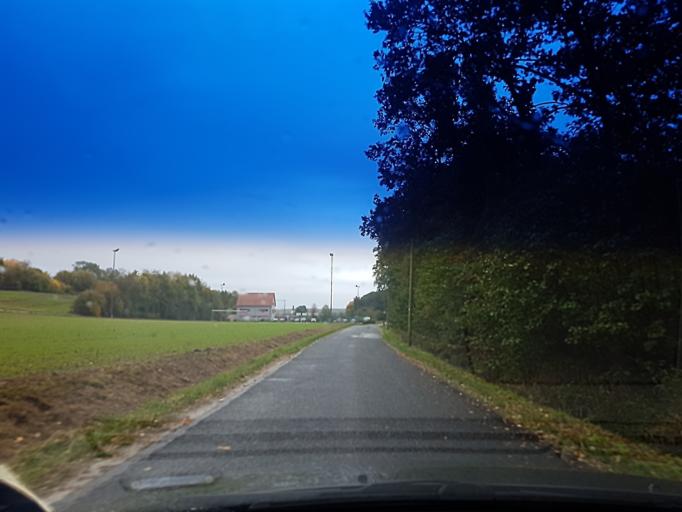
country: DE
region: Bavaria
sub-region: Regierungsbezirk Mittelfranken
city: Wachenroth
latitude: 49.7559
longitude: 10.6983
